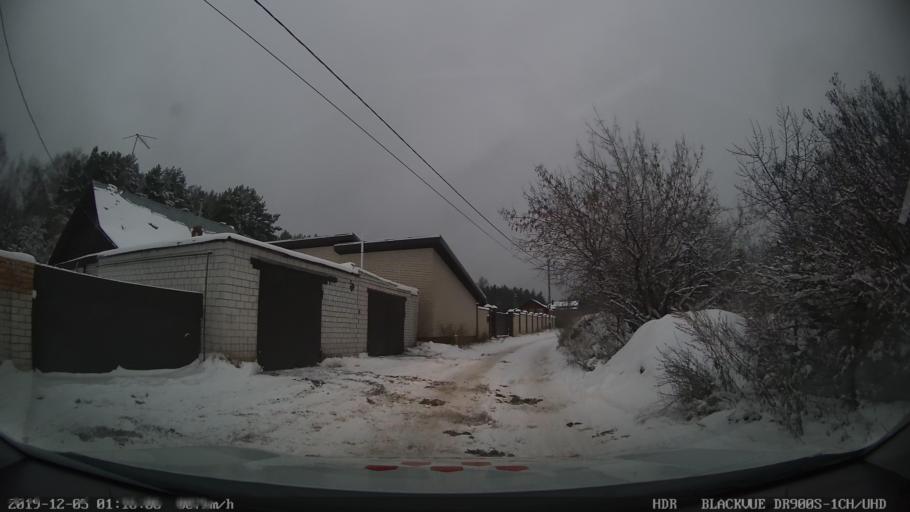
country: RU
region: Tatarstan
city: Stolbishchi
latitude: 55.6464
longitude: 49.1107
